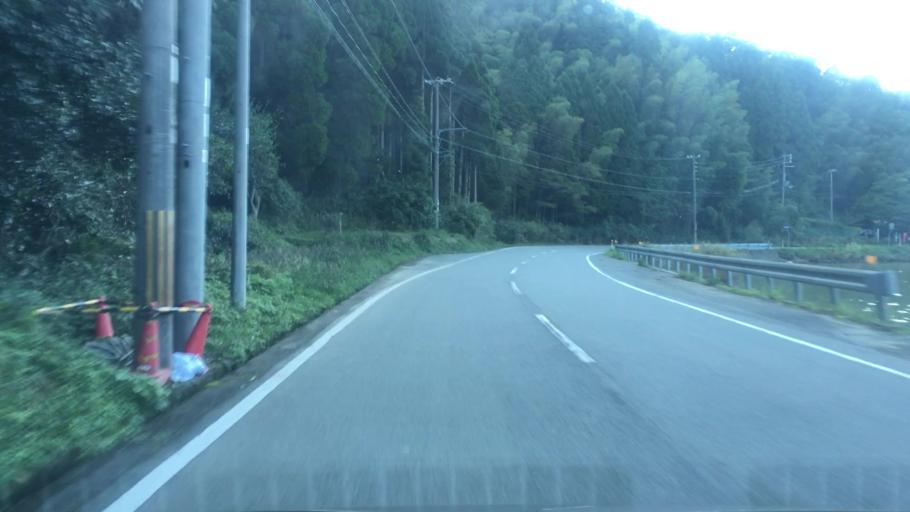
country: JP
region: Hyogo
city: Toyooka
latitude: 35.6161
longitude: 134.8251
